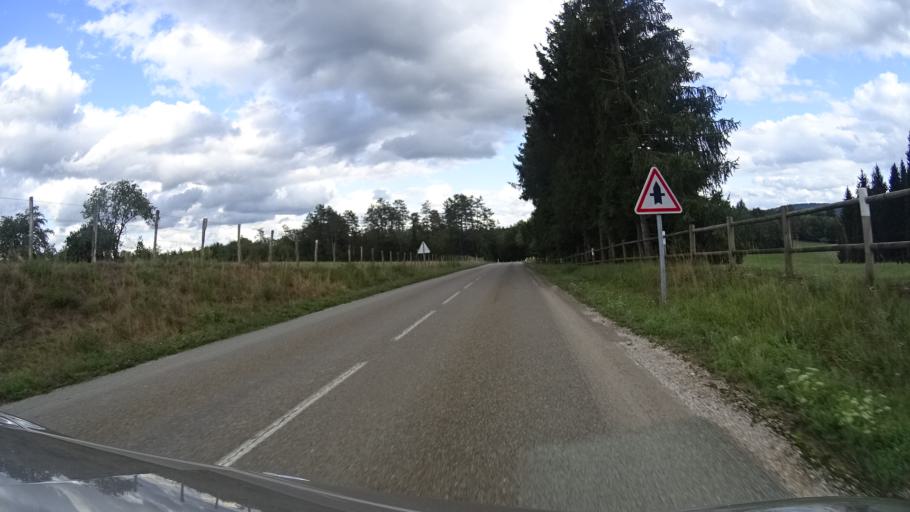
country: FR
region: Franche-Comte
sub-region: Departement du Doubs
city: Mamirolle
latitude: 47.2222
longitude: 6.1539
